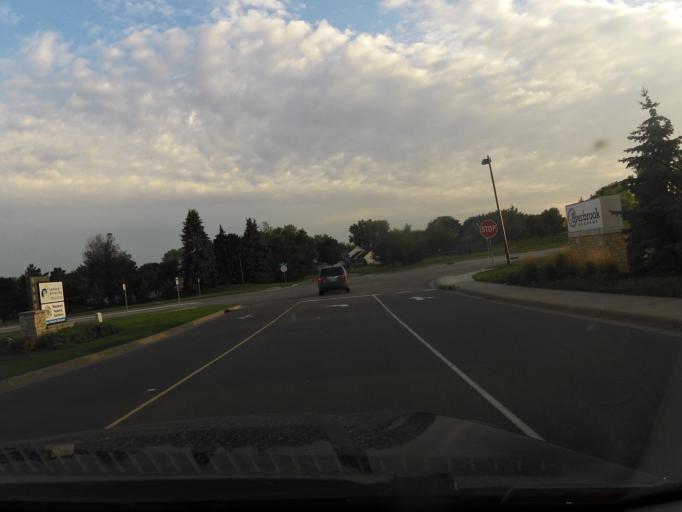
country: US
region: Minnesota
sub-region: Washington County
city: Woodbury
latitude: 44.9384
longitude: -92.9085
